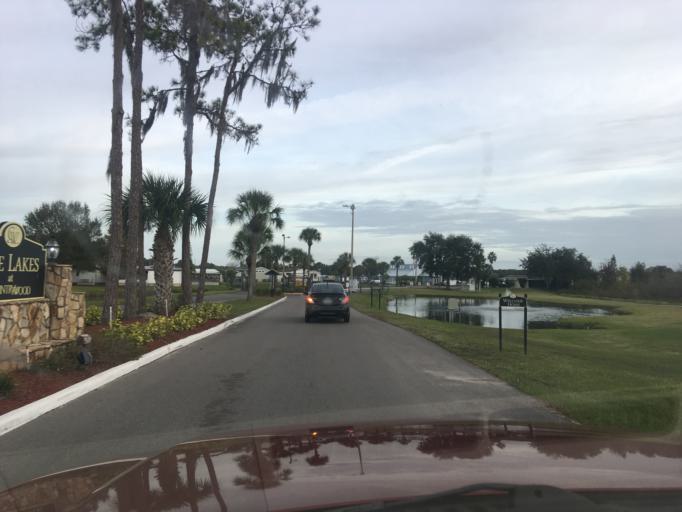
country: US
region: Florida
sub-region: Hillsborough County
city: Plant City
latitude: 28.0478
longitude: -82.1280
